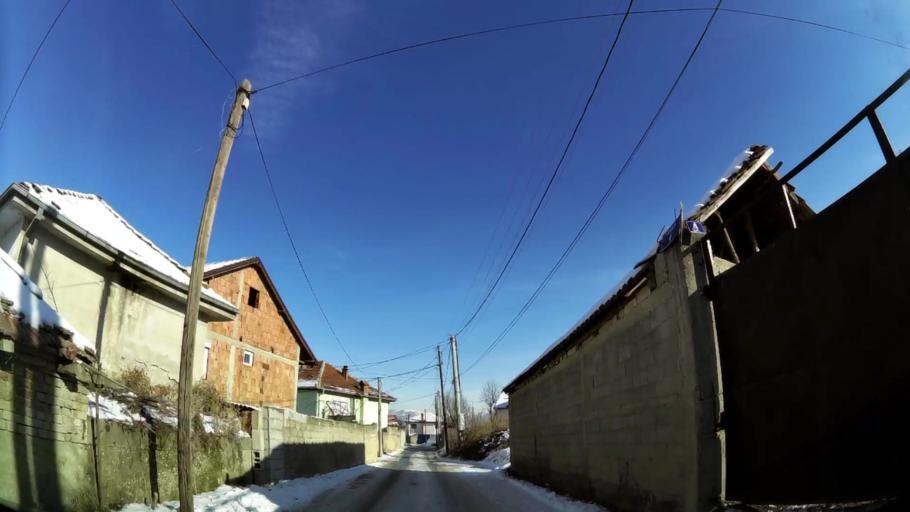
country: MK
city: Grchec
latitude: 41.9886
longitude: 21.3318
